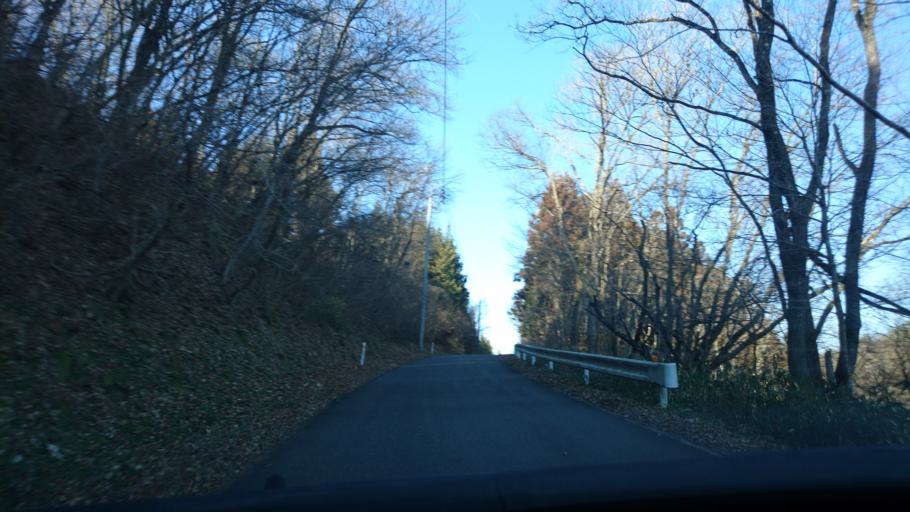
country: JP
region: Iwate
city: Ichinoseki
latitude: 38.8514
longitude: 141.2314
